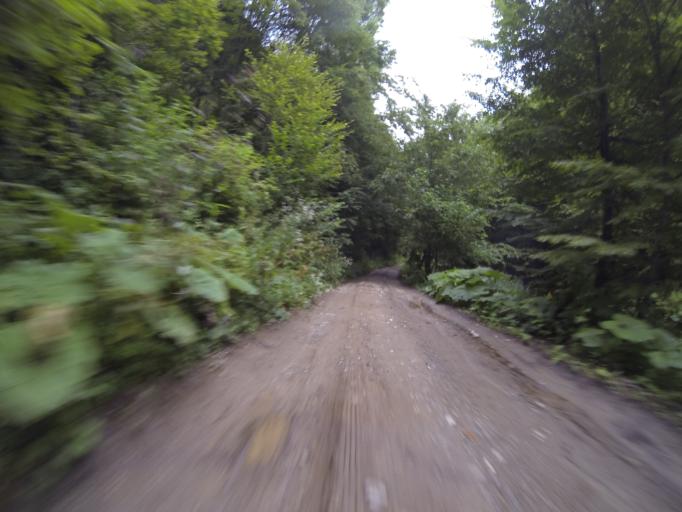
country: RO
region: Brasov
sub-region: Comuna Sinca Veche
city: Sinca Veche
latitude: 45.6847
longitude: 25.1382
